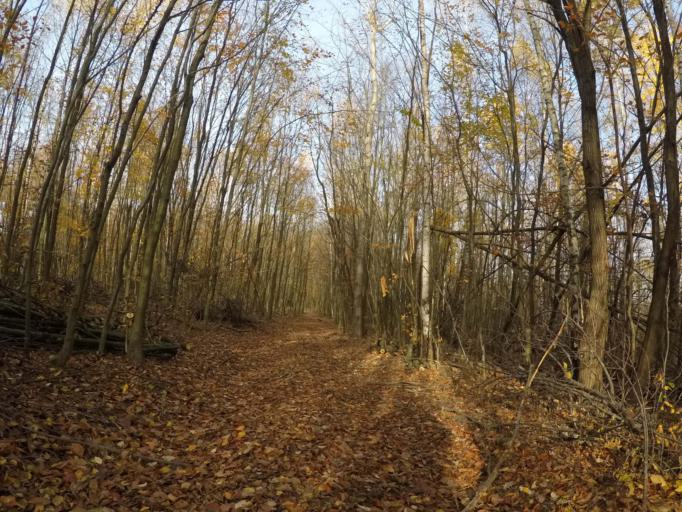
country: SK
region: Presovsky
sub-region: Okres Presov
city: Presov
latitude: 48.9126
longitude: 21.2127
